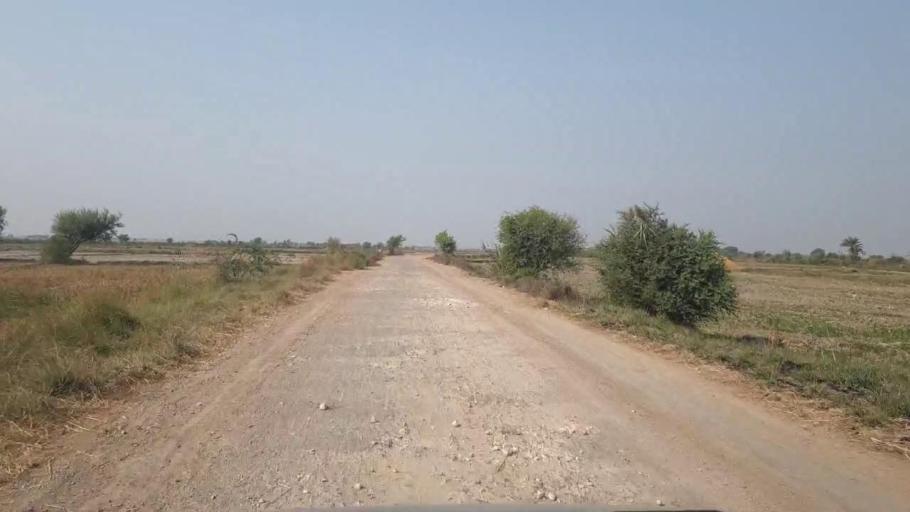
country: PK
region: Sindh
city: Tando Muhammad Khan
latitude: 25.0867
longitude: 68.3399
